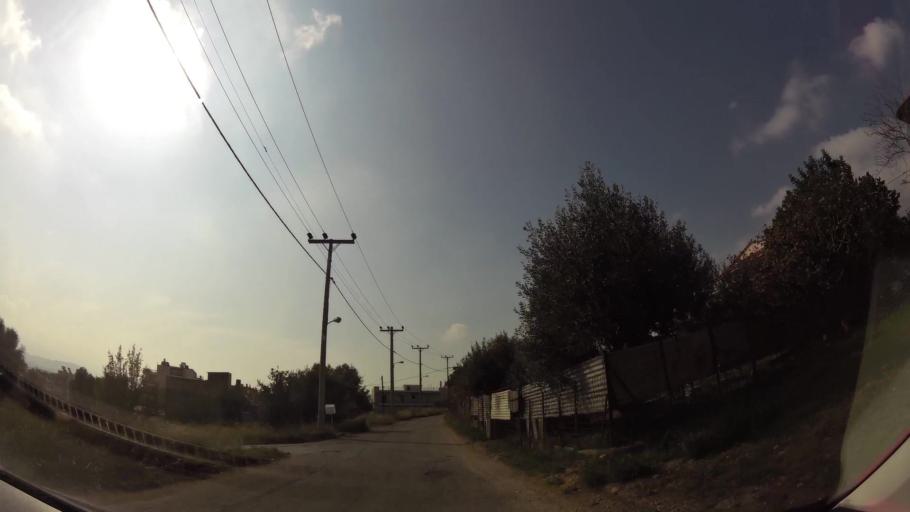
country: GR
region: Attica
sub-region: Nomarchia Dytikis Attikis
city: Zefyri
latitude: 38.0592
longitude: 23.7279
